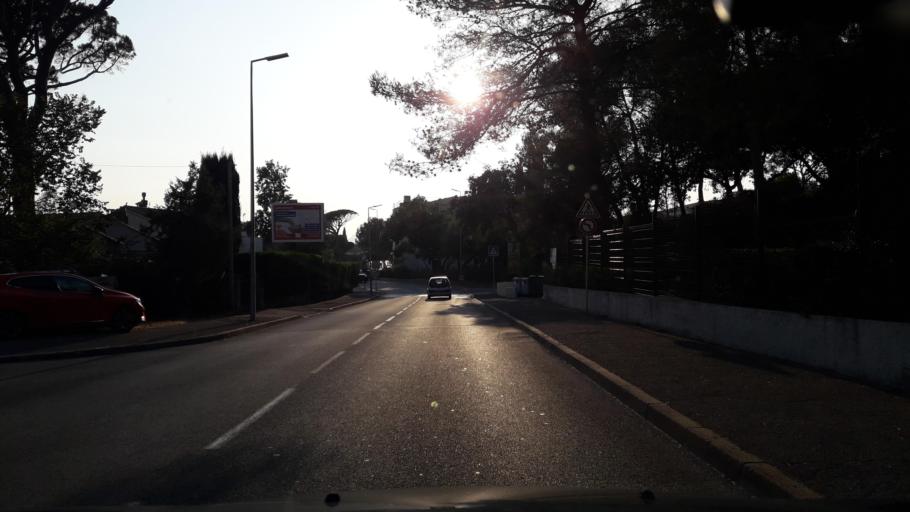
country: FR
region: Provence-Alpes-Cote d'Azur
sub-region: Departement du Var
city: Saint-Raphael
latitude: 43.4367
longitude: 6.7731
